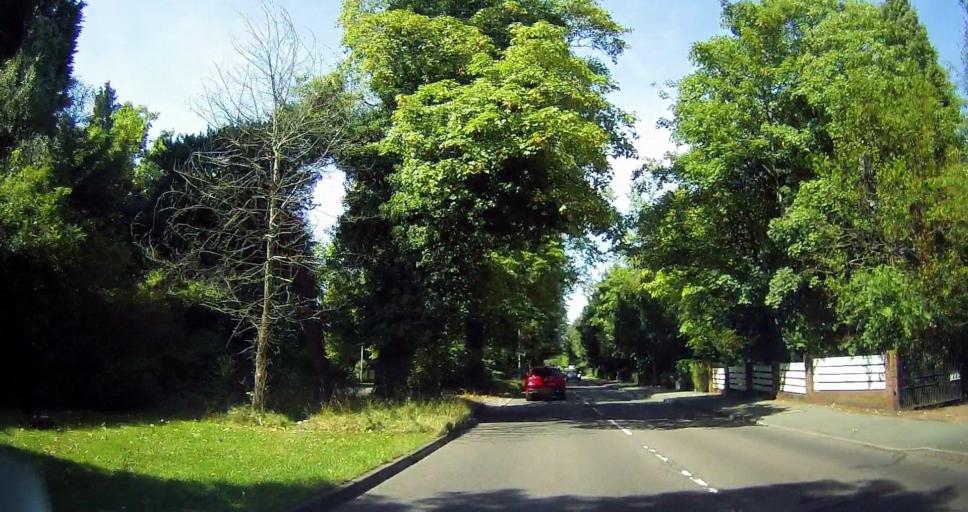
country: GB
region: England
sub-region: Staffordshire
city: Codsall
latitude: 52.6044
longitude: -2.1823
